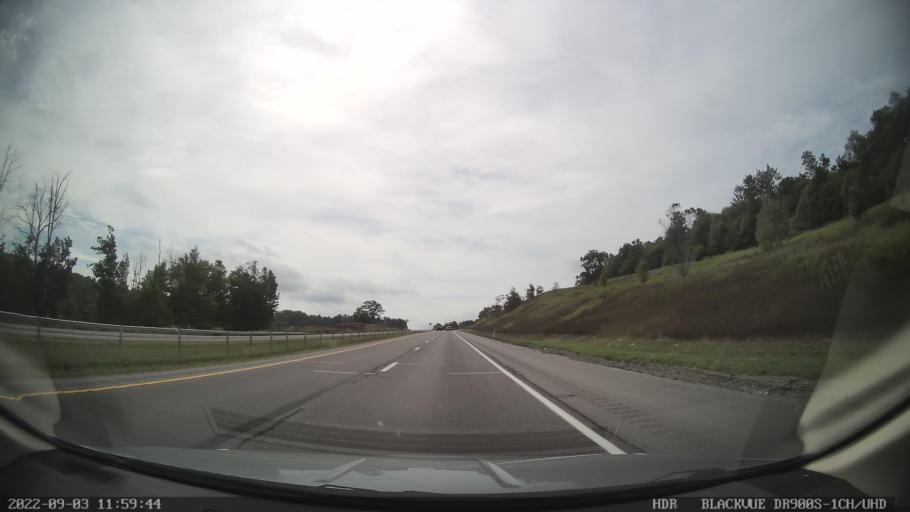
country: US
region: Pennsylvania
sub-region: Tioga County
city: Blossburg
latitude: 41.6248
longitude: -77.1188
